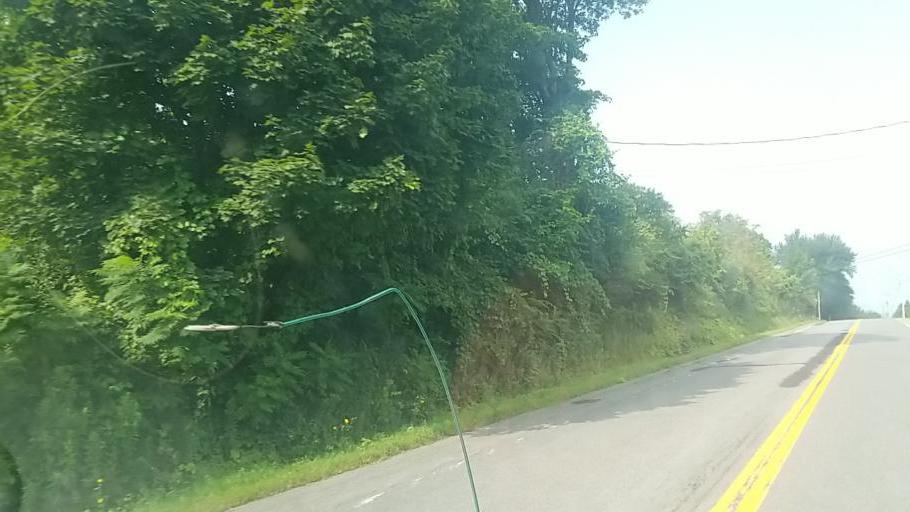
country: US
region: New York
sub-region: Fulton County
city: Johnstown
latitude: 43.0172
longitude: -74.3899
